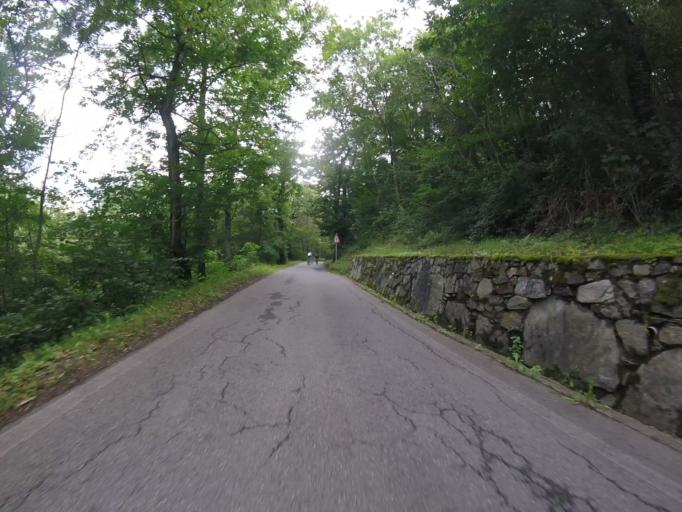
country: IT
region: Lombardy
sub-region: Provincia di Sondrio
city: Mazzo di Valtellina
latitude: 46.2530
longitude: 10.2614
